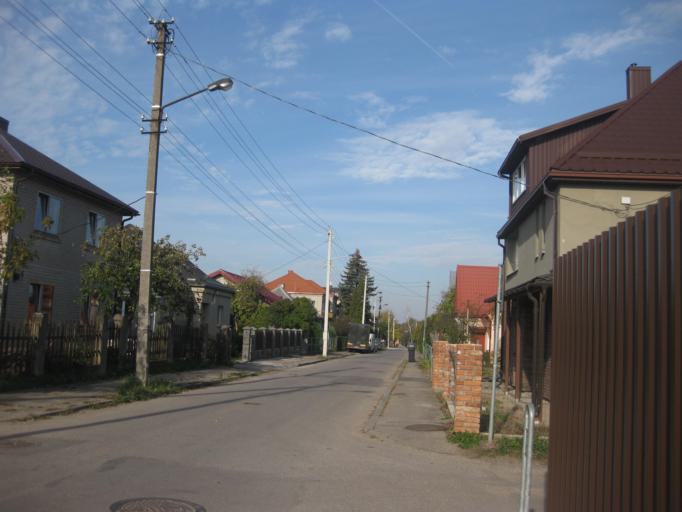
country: LT
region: Kauno apskritis
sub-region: Kaunas
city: Aleksotas
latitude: 54.8888
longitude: 23.8907
